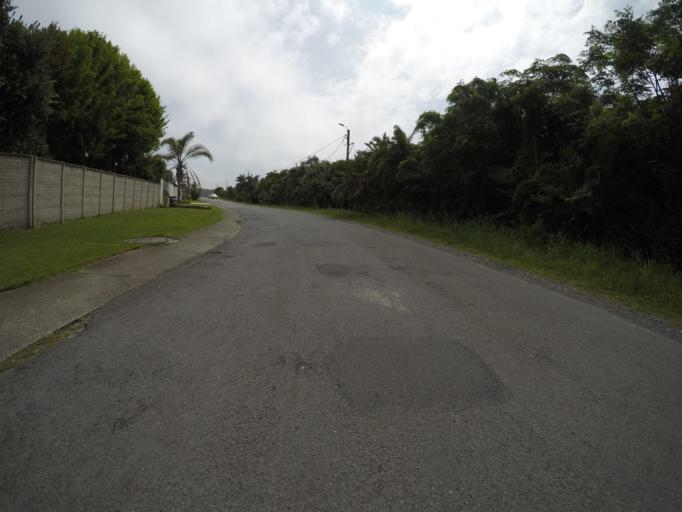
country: ZA
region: Eastern Cape
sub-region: Buffalo City Metropolitan Municipality
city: East London
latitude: -32.9374
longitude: 28.0274
